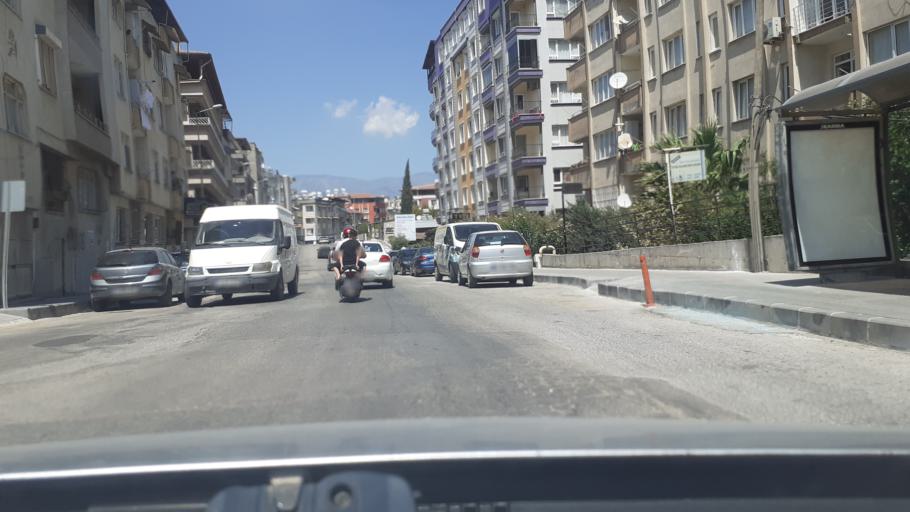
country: TR
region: Hatay
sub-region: Antakya Ilcesi
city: Antakya
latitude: 36.1968
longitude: 36.1553
